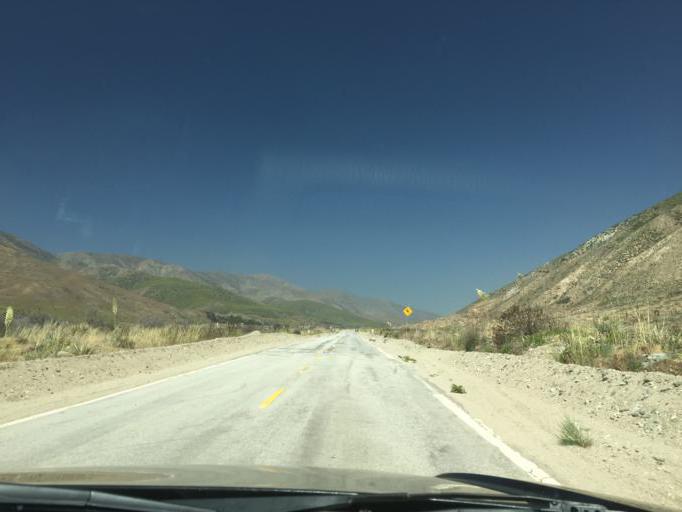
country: US
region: California
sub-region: San Bernardino County
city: Wrightwood
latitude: 34.3028
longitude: -117.5151
